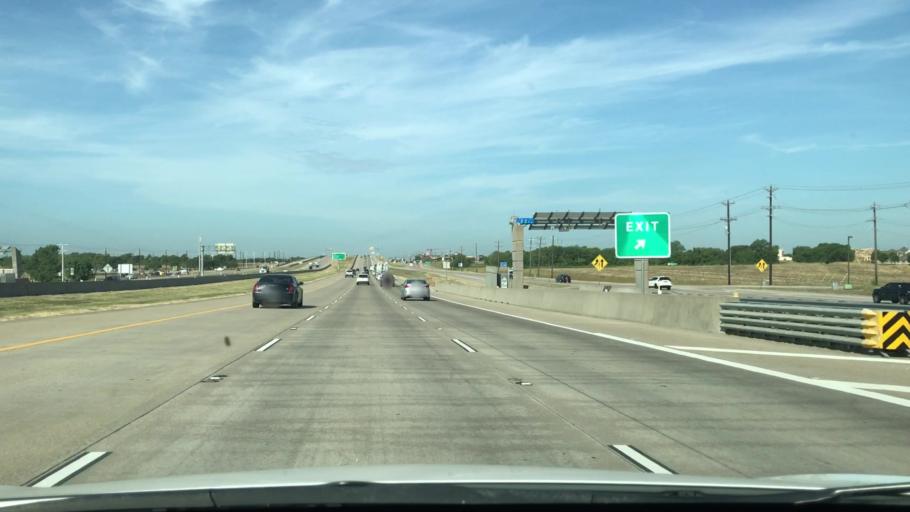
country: US
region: Texas
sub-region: Collin County
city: Allen
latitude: 33.1441
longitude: -96.6812
